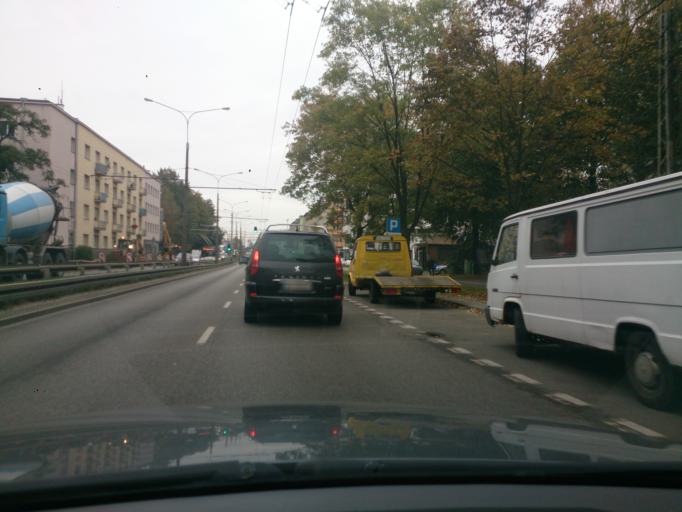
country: PL
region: Pomeranian Voivodeship
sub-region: Gdynia
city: Gdynia
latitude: 54.5305
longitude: 18.4980
